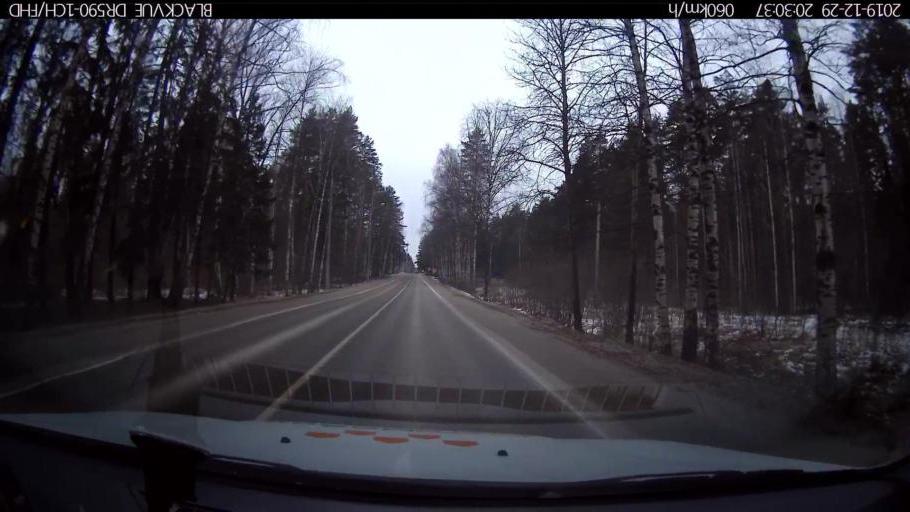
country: RU
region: Nizjnij Novgorod
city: Afonino
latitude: 56.1748
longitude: 44.0918
